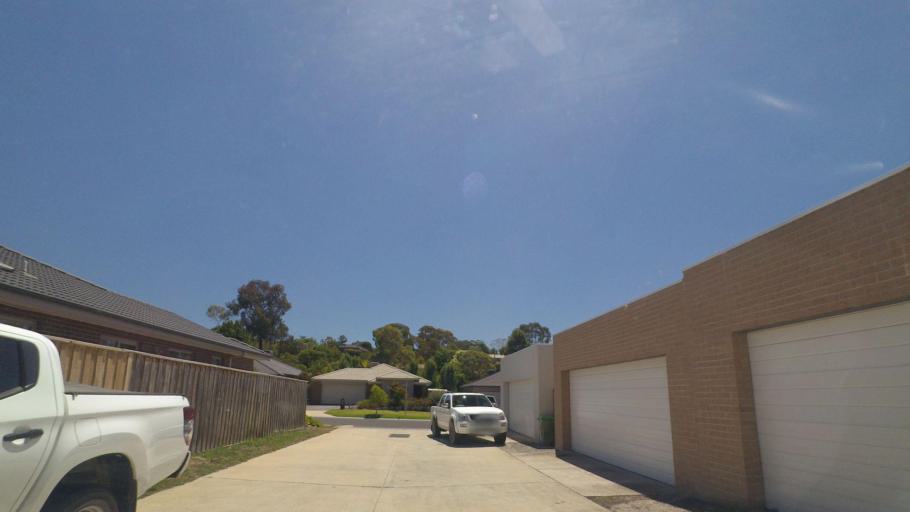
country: AU
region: Victoria
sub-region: Yarra Ranges
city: Lilydale
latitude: -37.7472
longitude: 145.3323
